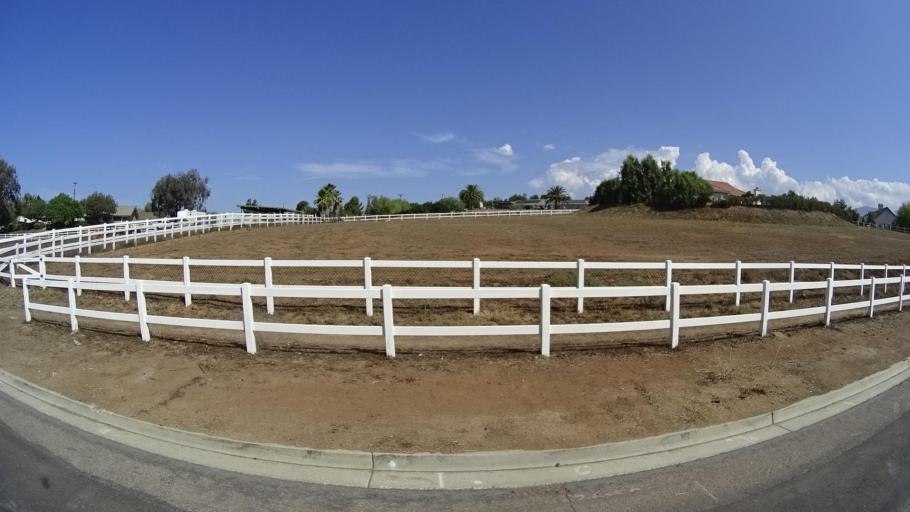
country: US
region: California
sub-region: San Diego County
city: Valley Center
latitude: 33.2820
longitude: -117.0212
